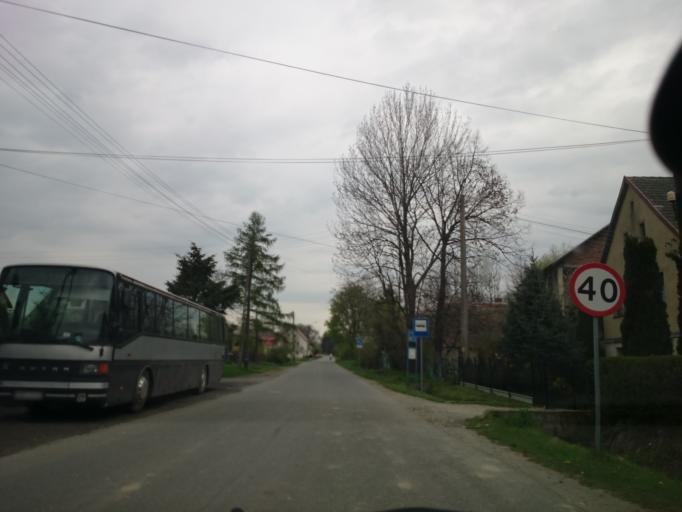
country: PL
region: Opole Voivodeship
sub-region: Powiat nyski
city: Glucholazy
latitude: 50.3201
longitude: 17.4326
